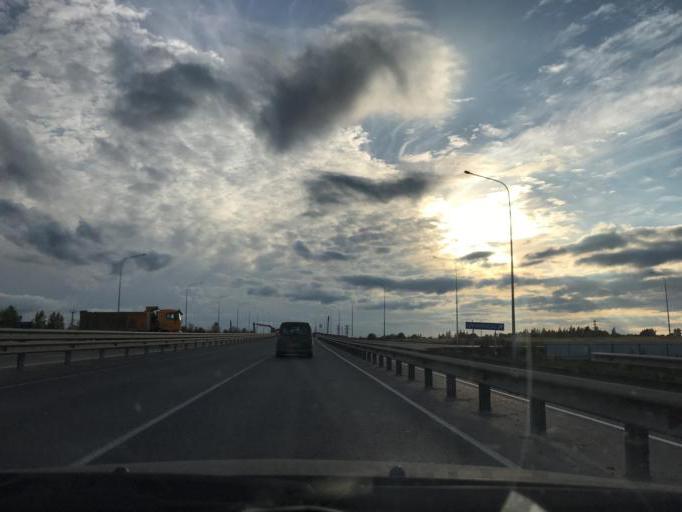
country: RU
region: Kaluga
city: Kurovskoye
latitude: 54.5363
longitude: 35.9999
